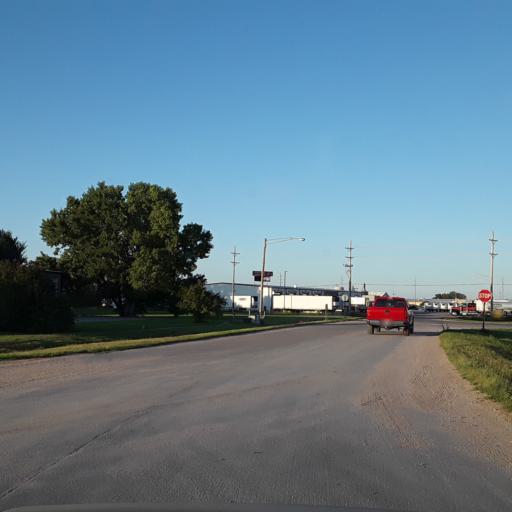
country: US
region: Nebraska
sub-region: Hall County
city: Grand Island
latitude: 40.9318
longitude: -98.3220
